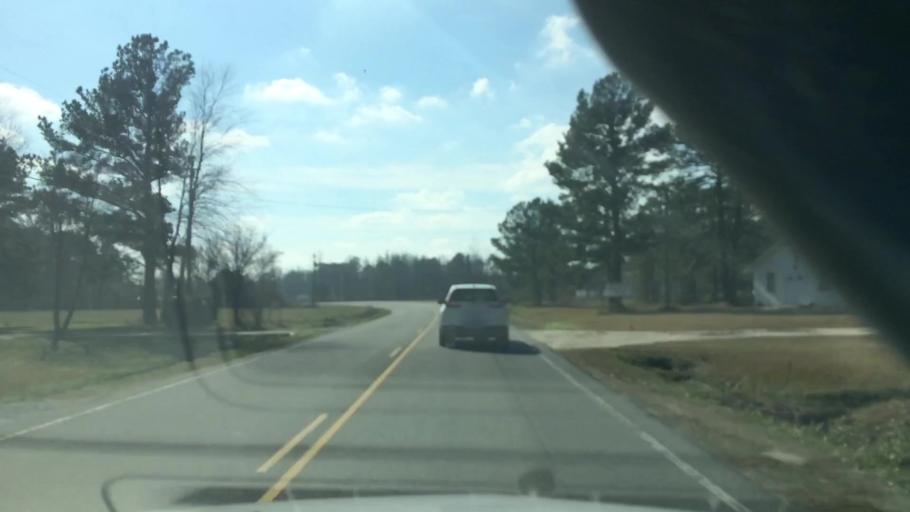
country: US
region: North Carolina
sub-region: Duplin County
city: Beulaville
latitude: 34.8827
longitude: -77.7882
